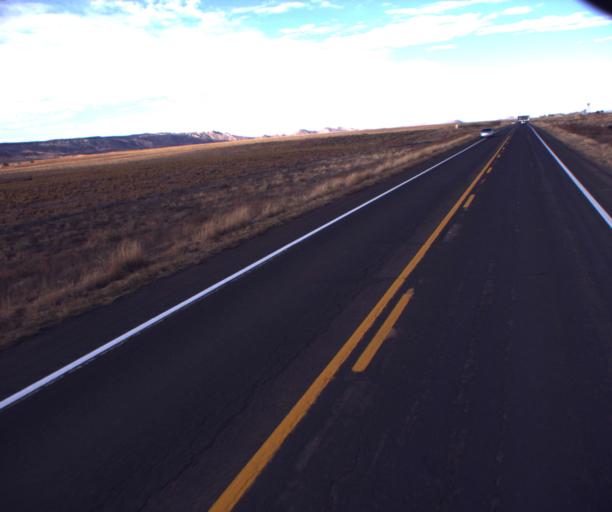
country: US
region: Arizona
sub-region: Apache County
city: Lukachukai
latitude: 36.9600
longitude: -109.3572
